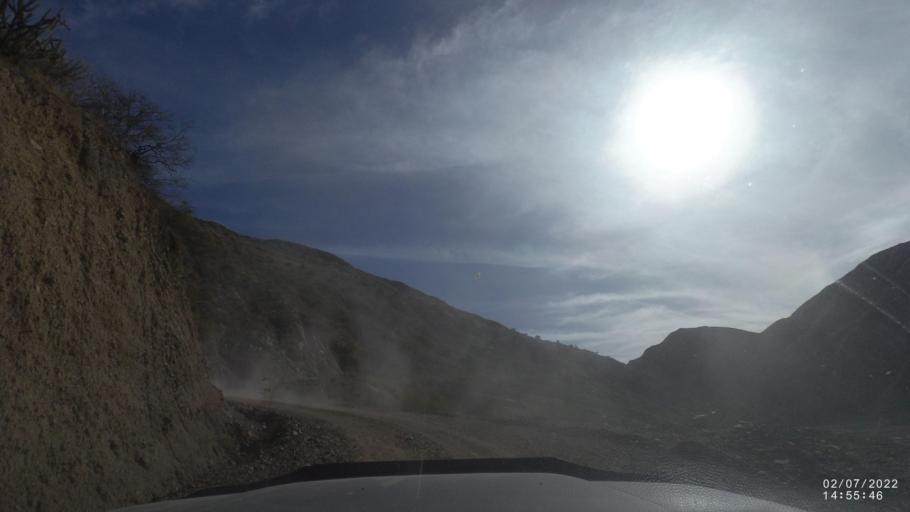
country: BO
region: Cochabamba
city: Irpa Irpa
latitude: -17.8560
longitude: -66.4336
